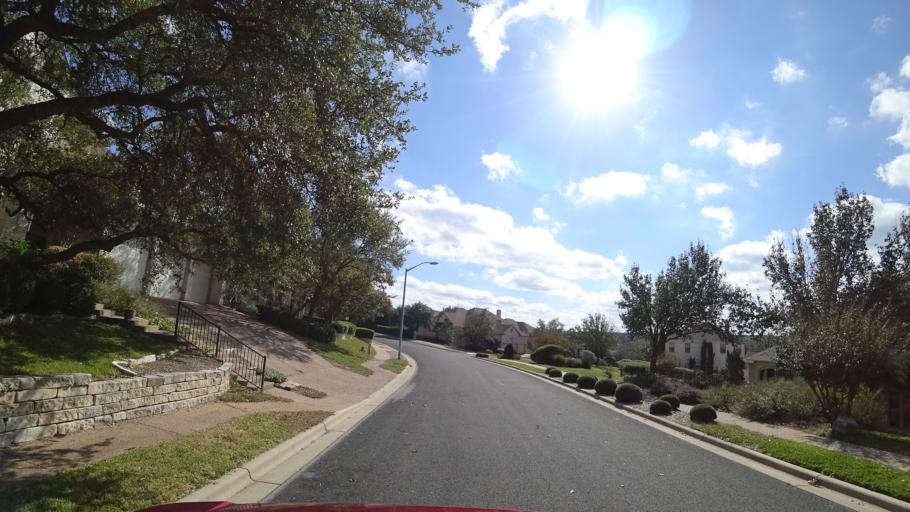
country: US
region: Texas
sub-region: Williamson County
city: Anderson Mill
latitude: 30.4250
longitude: -97.8072
